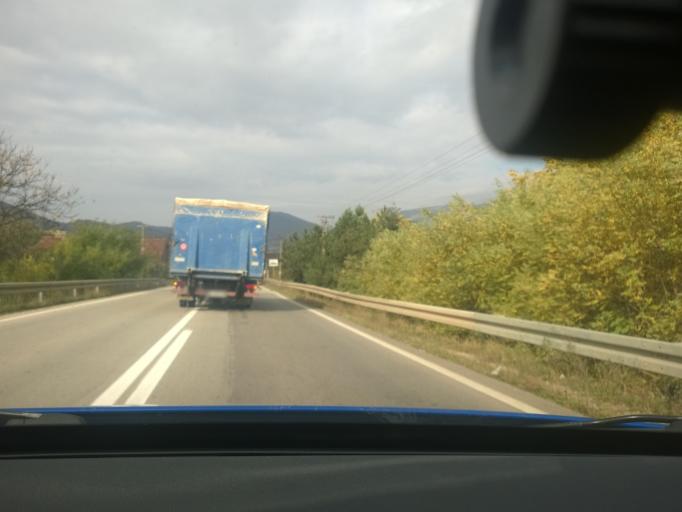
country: RS
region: Central Serbia
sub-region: Pirotski Okrug
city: Bela Palanka
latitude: 43.2942
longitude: 22.2090
